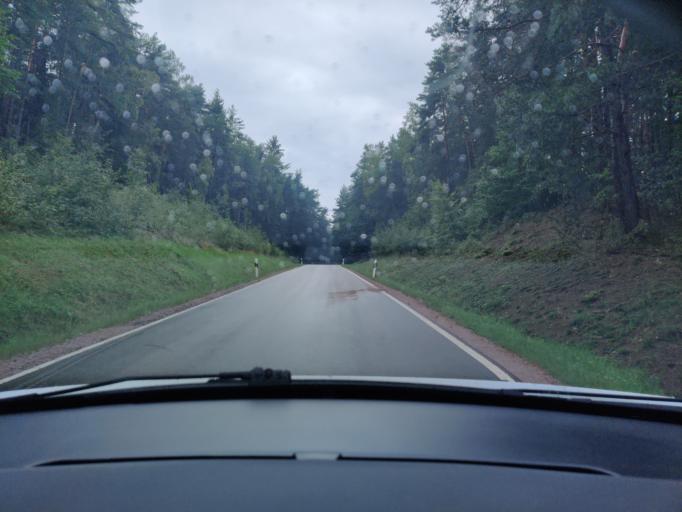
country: DE
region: Bavaria
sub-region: Upper Palatinate
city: Pfreimd
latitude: 49.5007
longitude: 12.1583
